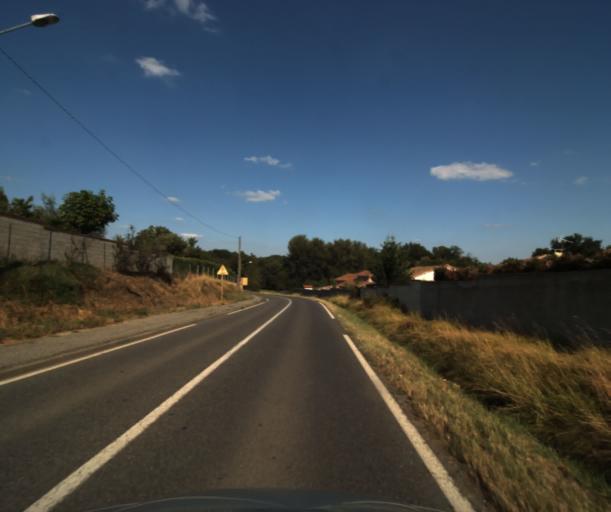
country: FR
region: Midi-Pyrenees
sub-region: Departement de la Haute-Garonne
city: Saint-Lys
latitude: 43.5114
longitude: 1.1909
